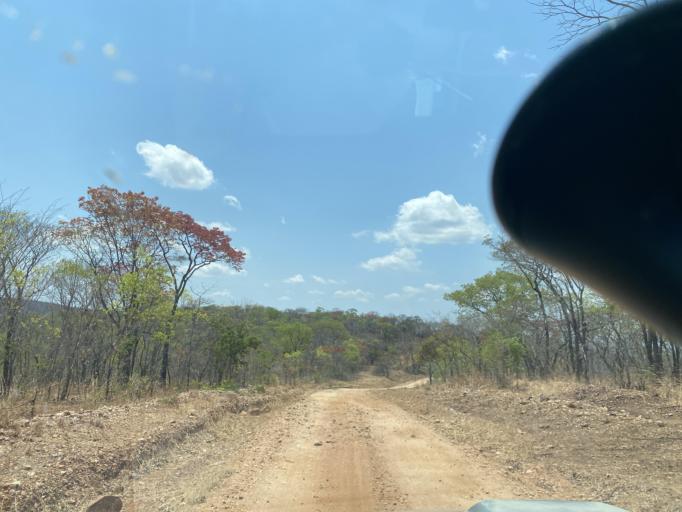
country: ZM
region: Lusaka
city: Luangwa
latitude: -15.0077
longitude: 29.7333
